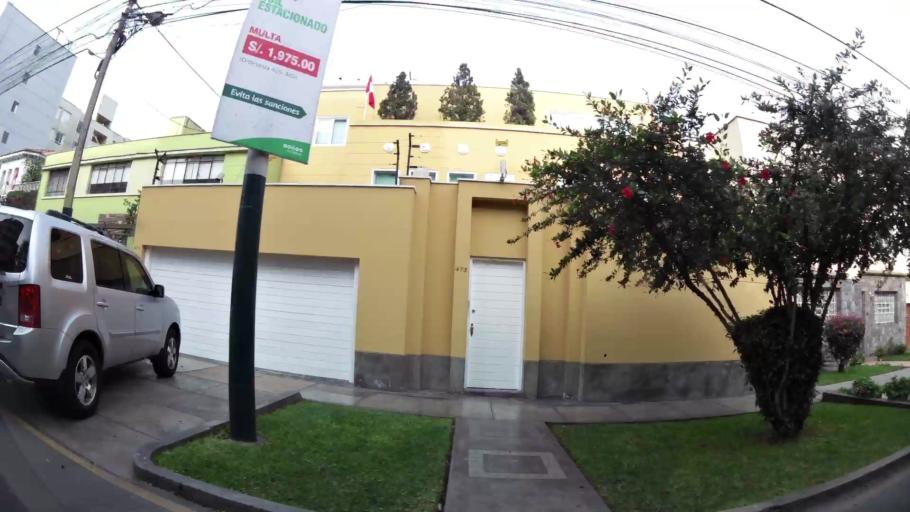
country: PE
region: Lima
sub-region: Lima
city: San Isidro
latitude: -12.0962
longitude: -77.0561
